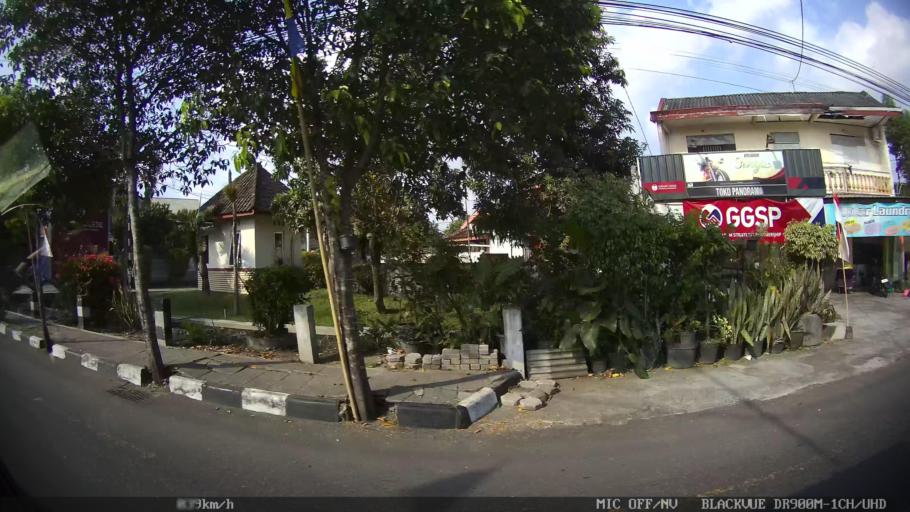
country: ID
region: Daerah Istimewa Yogyakarta
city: Yogyakarta
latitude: -7.8198
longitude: 110.3882
